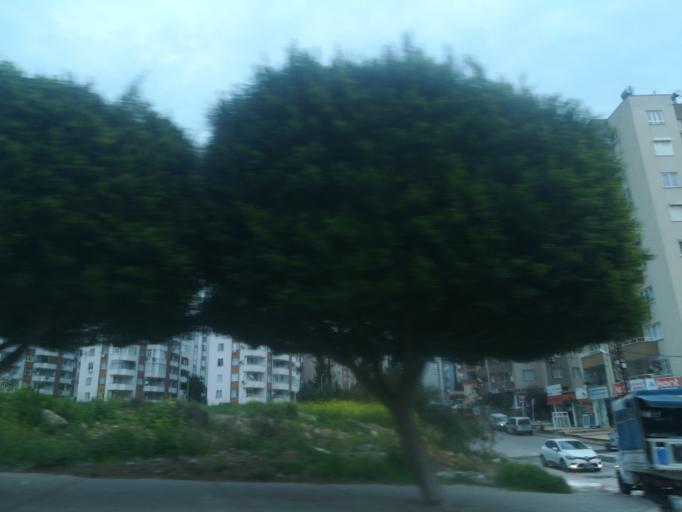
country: TR
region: Adana
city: Adana
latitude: 37.0415
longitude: 35.2922
